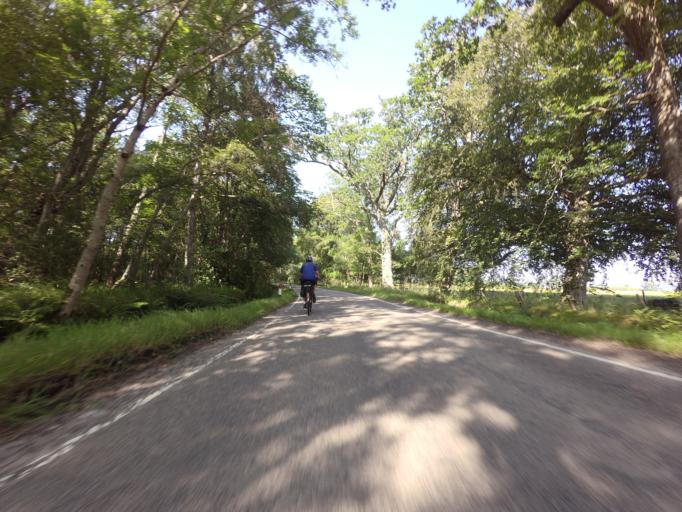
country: GB
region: Scotland
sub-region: Highland
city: Evanton
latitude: 57.6470
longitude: -4.3520
